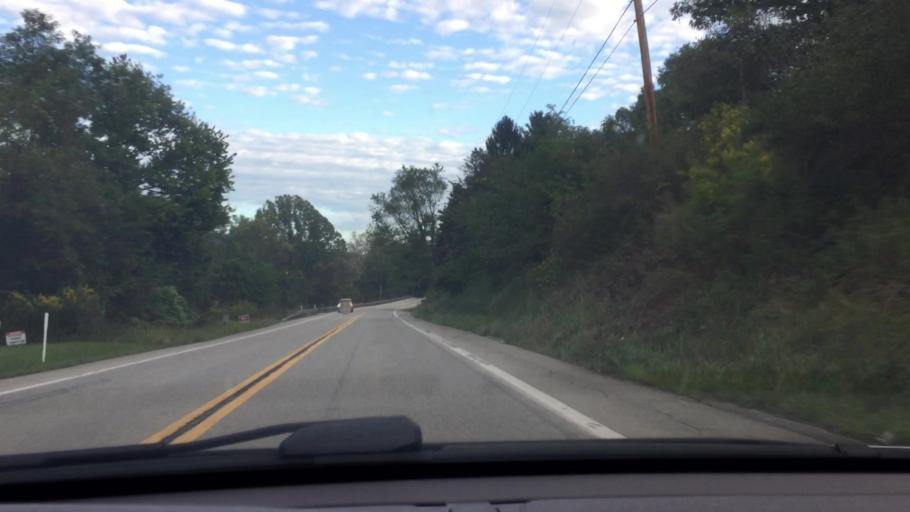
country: US
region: Pennsylvania
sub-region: Washington County
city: McGovern
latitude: 40.1703
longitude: -80.1350
